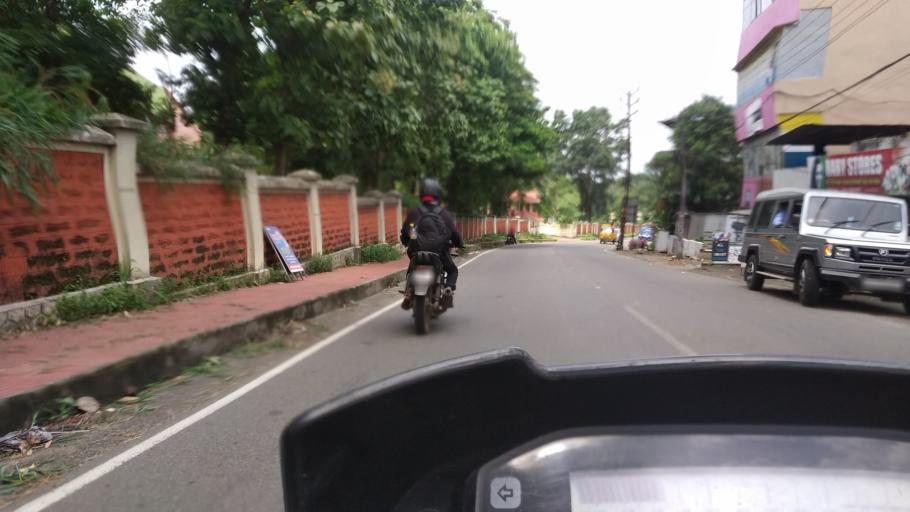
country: IN
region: Kerala
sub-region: Ernakulam
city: Aluva
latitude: 10.1244
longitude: 76.3345
